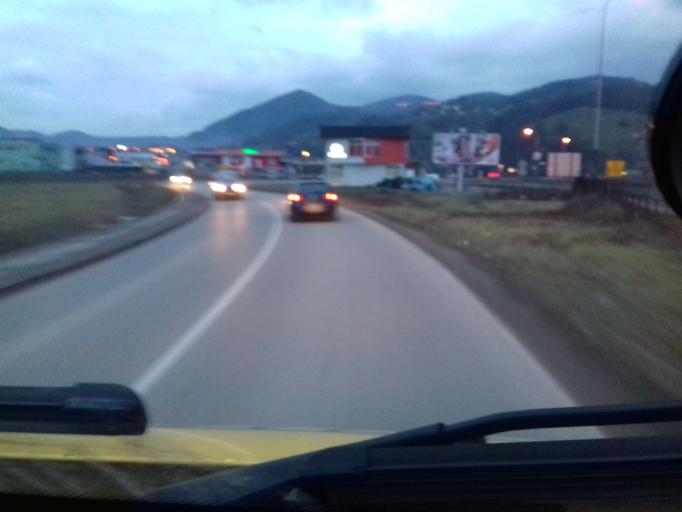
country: BA
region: Federation of Bosnia and Herzegovina
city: Visoko
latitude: 44.0011
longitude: 18.1666
